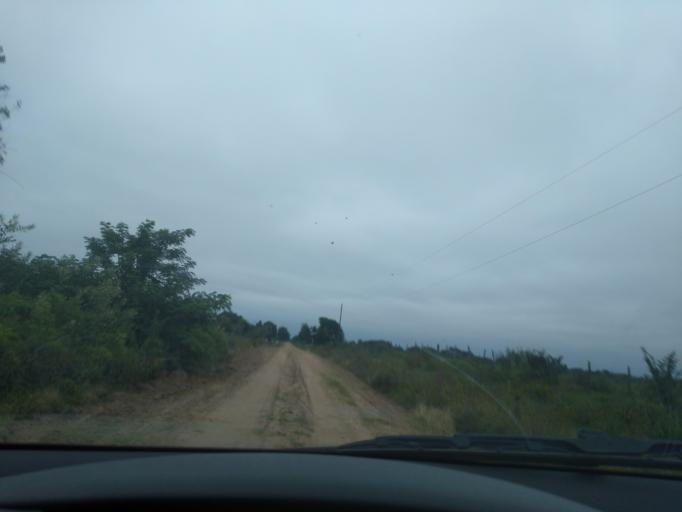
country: AR
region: Chaco
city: Colonia Benitez
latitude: -27.3620
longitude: -58.9578
